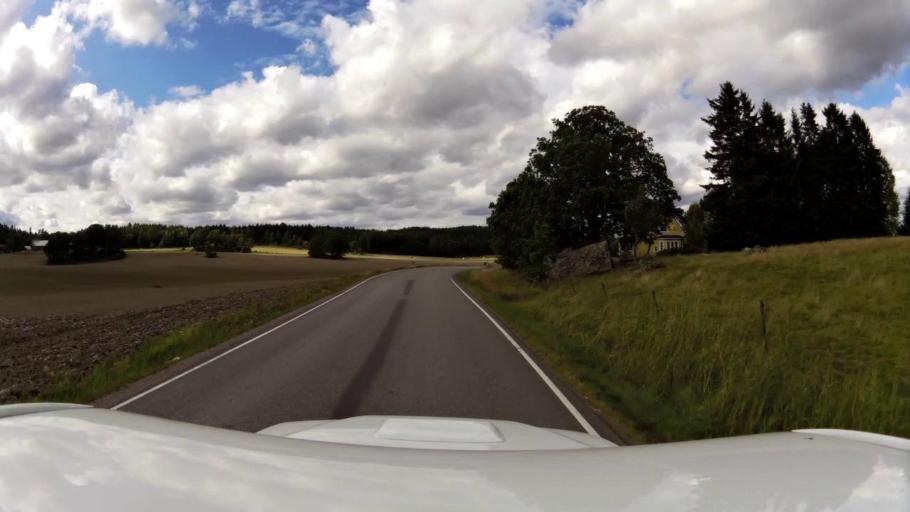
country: SE
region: OEstergoetland
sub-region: Linkopings Kommun
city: Sturefors
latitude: 58.3137
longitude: 15.7231
